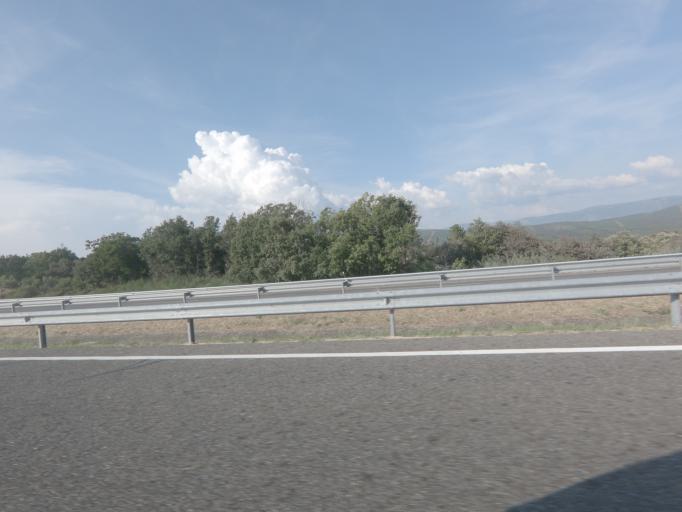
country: ES
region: Galicia
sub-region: Provincia de Ourense
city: Cualedro
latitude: 41.9670
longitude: -7.5293
